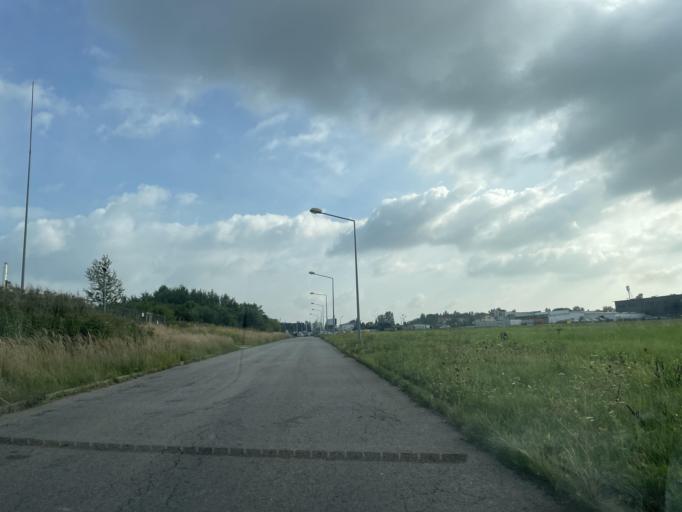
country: PL
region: Silesian Voivodeship
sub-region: Powiat bedzinski
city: Bedzin
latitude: 50.3029
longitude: 19.1702
